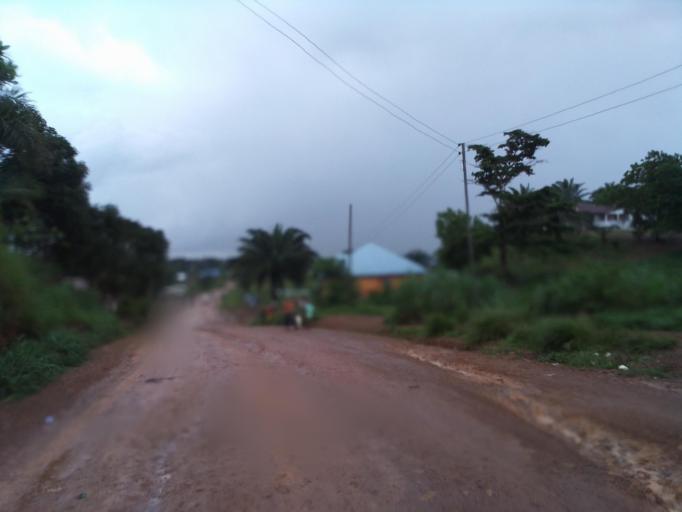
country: SL
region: Eastern Province
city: Kenema
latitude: 7.8762
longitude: -11.1624
